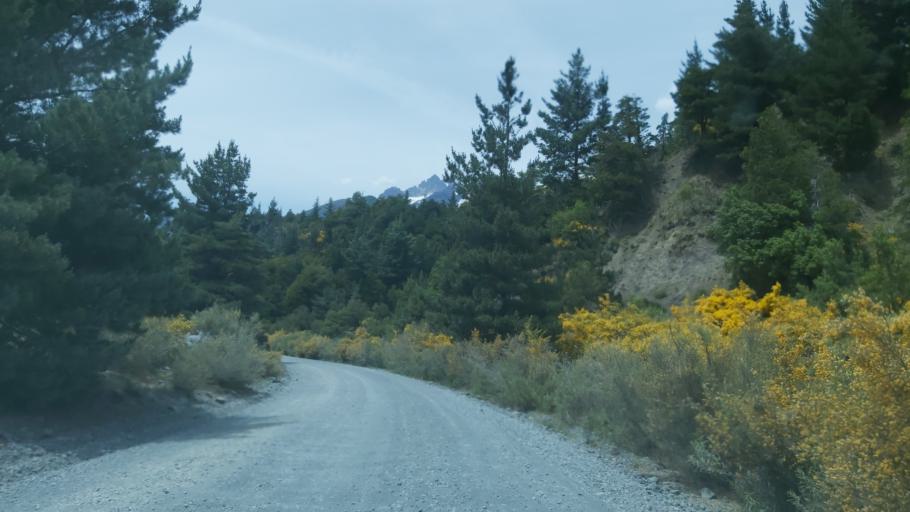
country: AR
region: Neuquen
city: Las Ovejas
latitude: -37.3903
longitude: -71.4667
